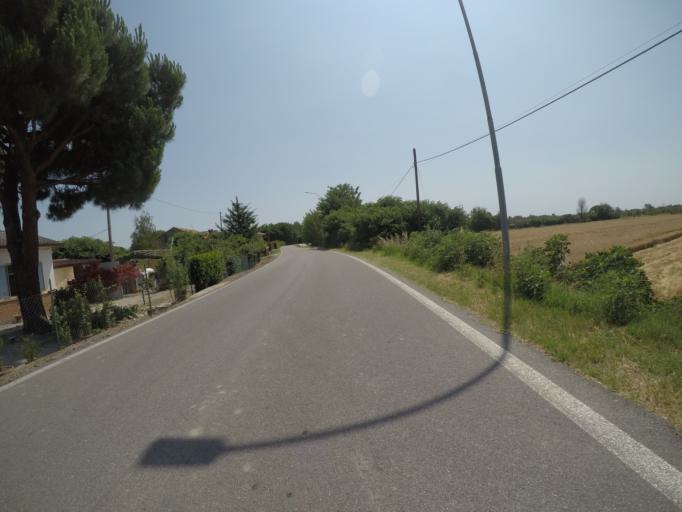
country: IT
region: Veneto
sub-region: Provincia di Rovigo
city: Villamarzana
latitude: 45.0077
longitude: 11.6720
